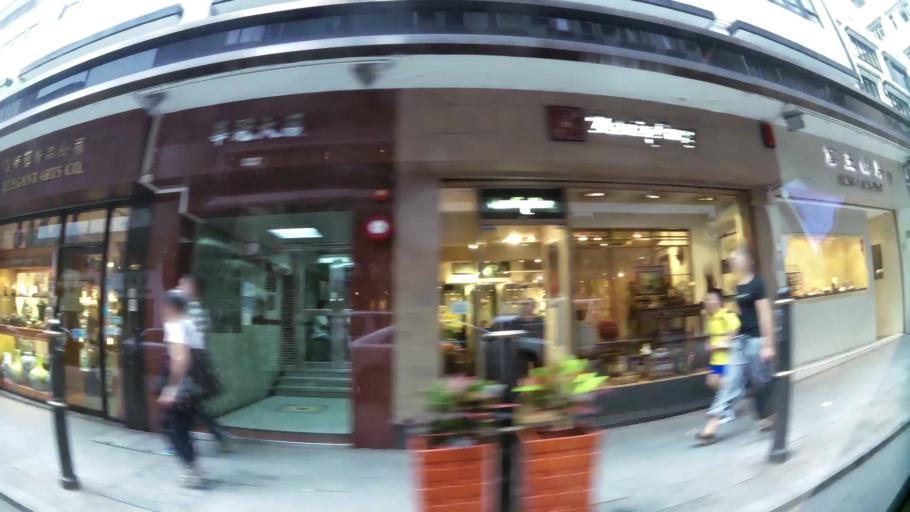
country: HK
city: Hong Kong
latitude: 22.2852
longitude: 114.1489
